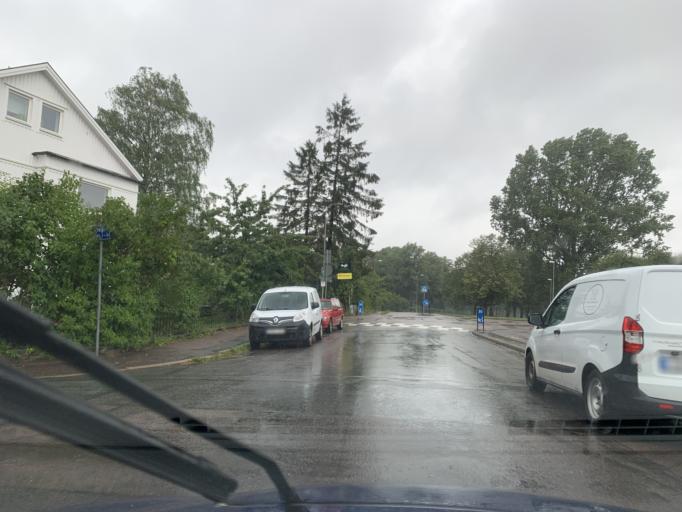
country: SE
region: Vaestra Goetaland
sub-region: Goteborg
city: Goeteborg
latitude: 57.7128
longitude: 12.0203
